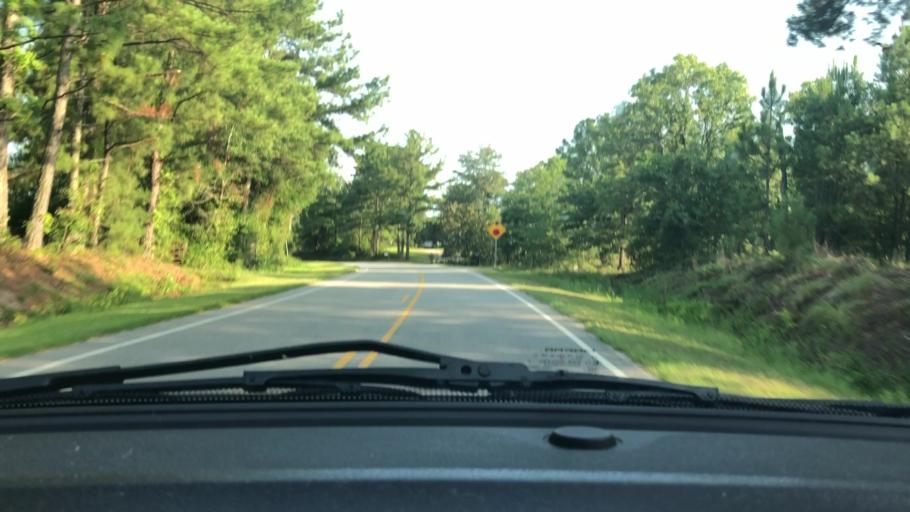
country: US
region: North Carolina
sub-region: Lee County
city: Broadway
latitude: 35.3261
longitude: -79.0717
